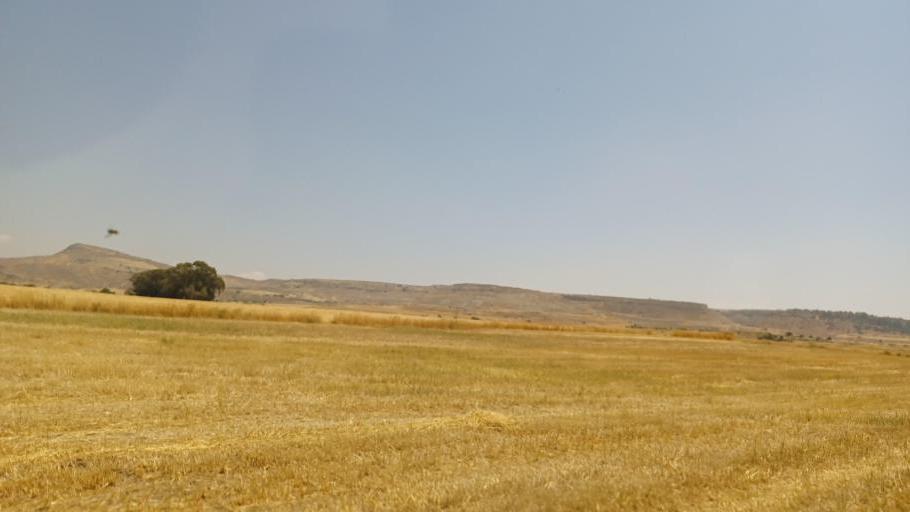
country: CY
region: Larnaka
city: Voroklini
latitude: 34.9842
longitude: 33.6270
